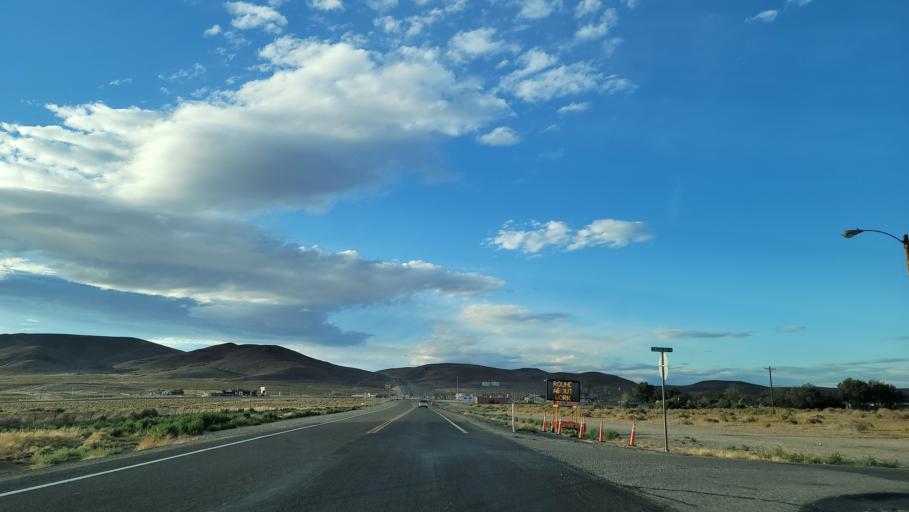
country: US
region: Nevada
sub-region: Lyon County
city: Silver Springs
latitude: 39.4092
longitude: -119.2264
